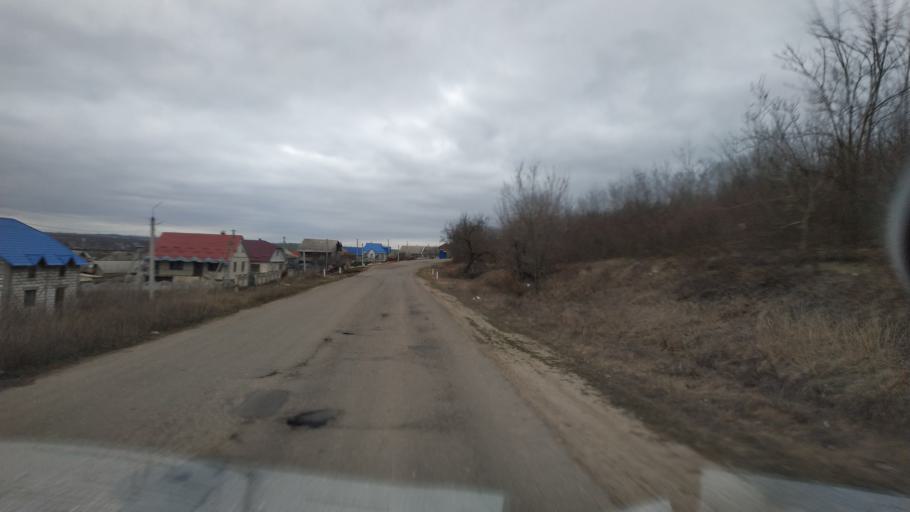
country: MD
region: Causeni
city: Causeni
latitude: 46.6615
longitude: 29.4481
